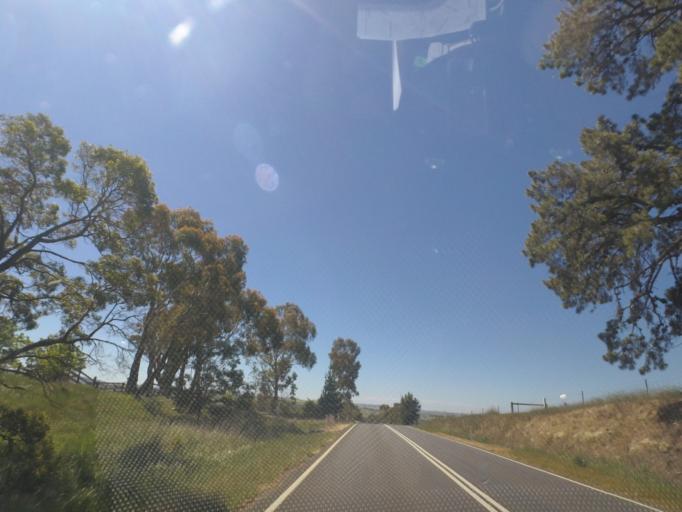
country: AU
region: Victoria
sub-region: Hume
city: Sunbury
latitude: -37.1880
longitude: 144.7395
